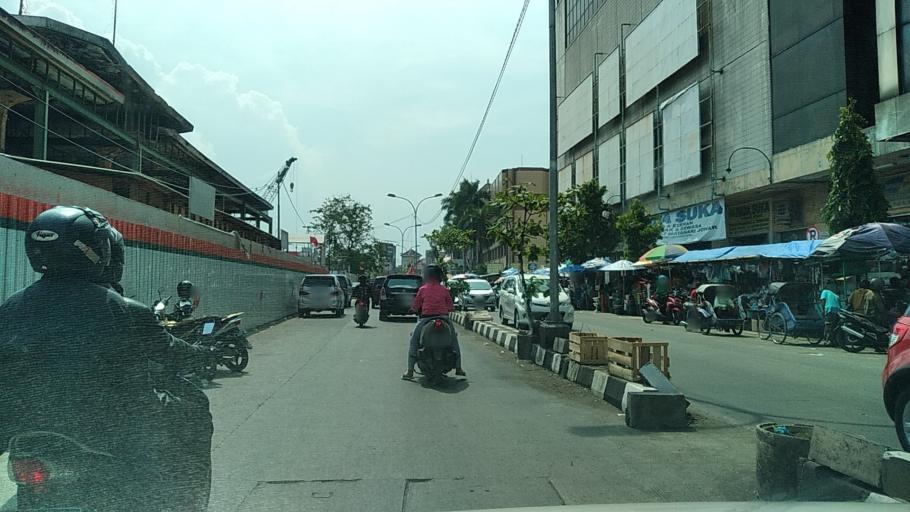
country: ID
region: Central Java
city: Semarang
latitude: -6.9714
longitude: 110.4250
